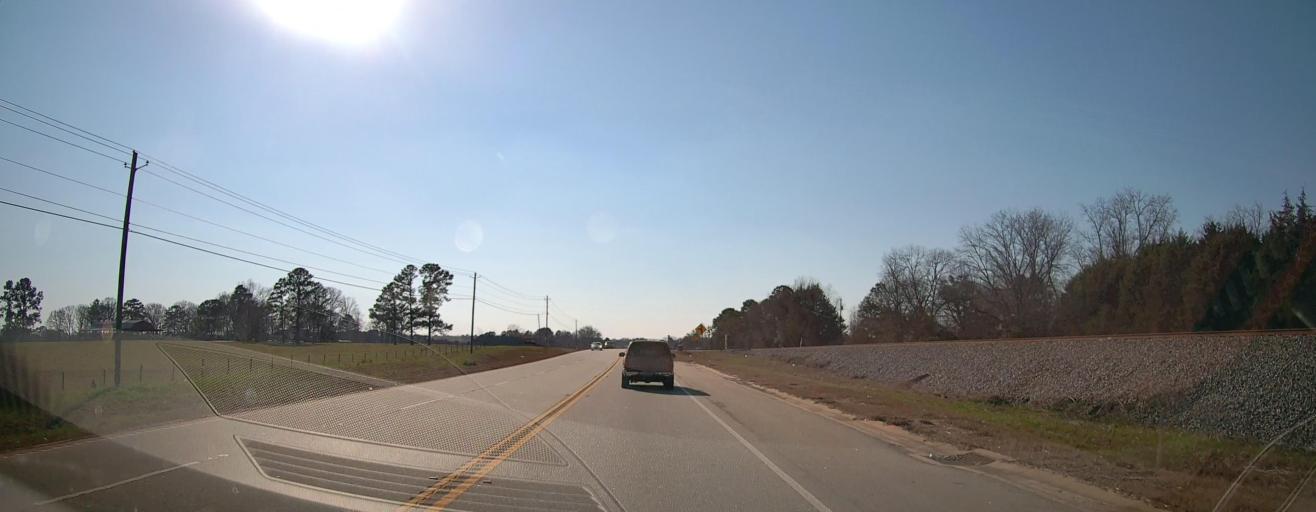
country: US
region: Georgia
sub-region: Butts County
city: Jackson
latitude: 33.3259
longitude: -84.0105
